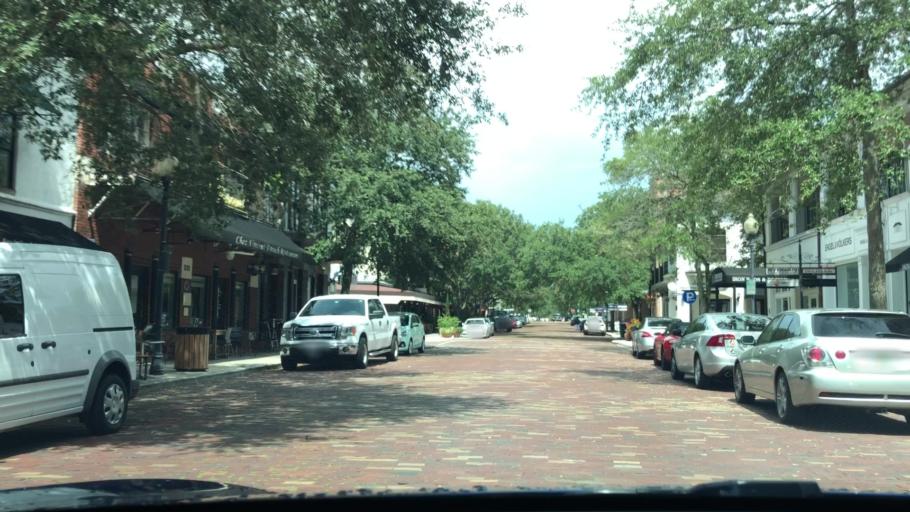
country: US
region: Florida
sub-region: Orange County
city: Winter Park
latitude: 28.5958
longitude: -81.3568
